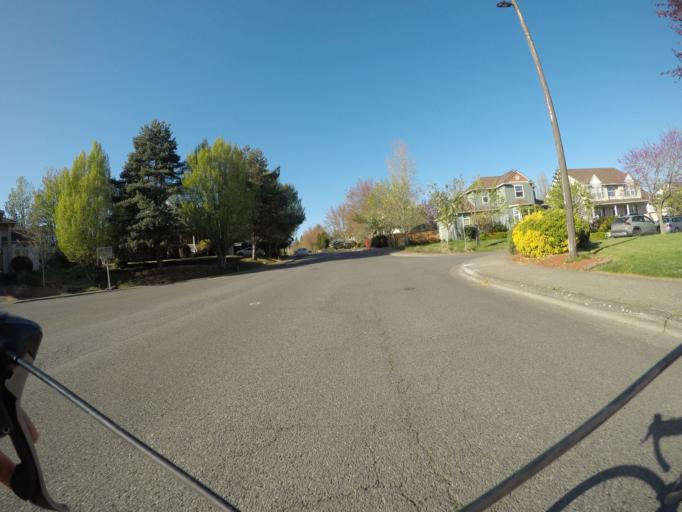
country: US
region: Oregon
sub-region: Washington County
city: King City
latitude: 45.4248
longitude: -122.8450
